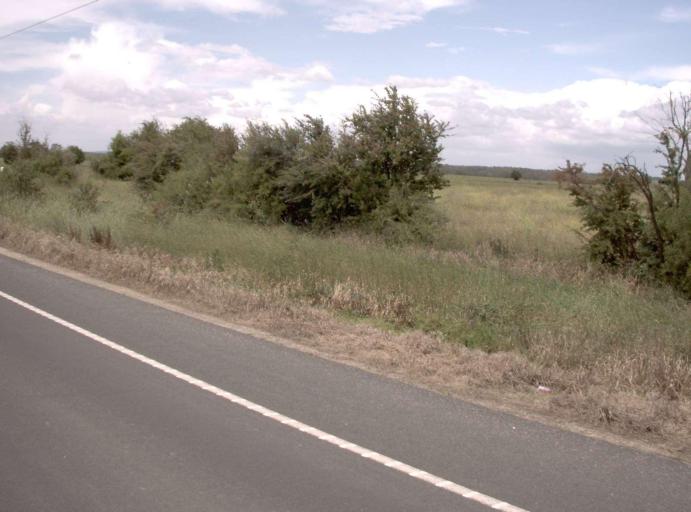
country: AU
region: Victoria
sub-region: Wellington
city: Sale
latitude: -38.0420
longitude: 147.0196
